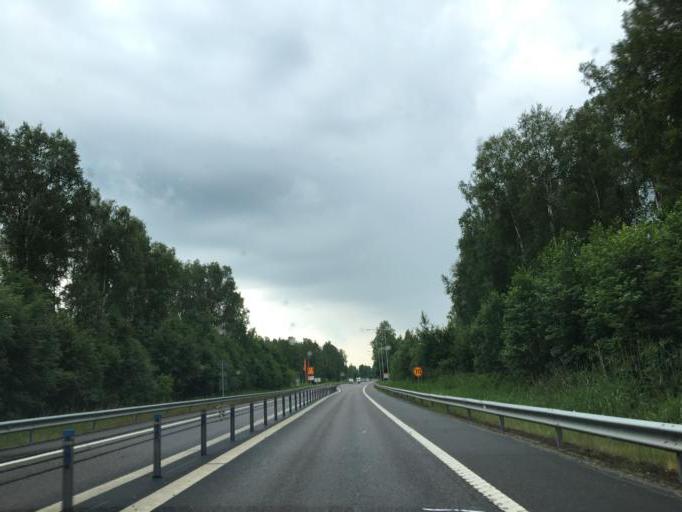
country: SE
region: OEstergoetland
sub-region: Norrkopings Kommun
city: Jursla
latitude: 58.7902
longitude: 16.1564
